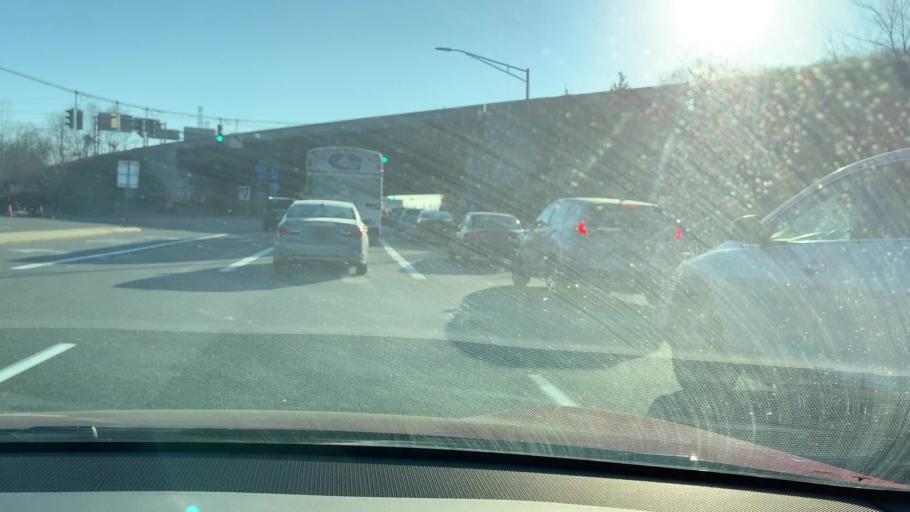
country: US
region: New York
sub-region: Westchester County
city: Elmsford
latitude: 41.0598
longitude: -73.8303
